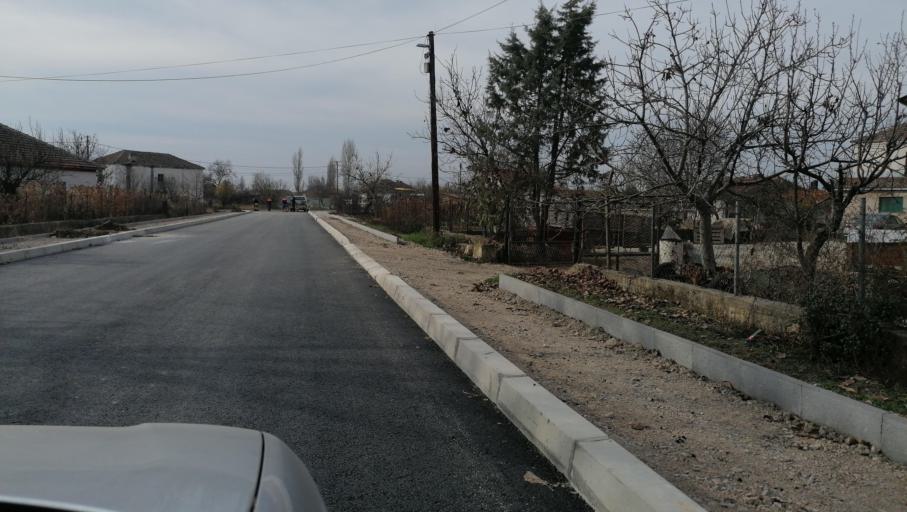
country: MK
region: Cesinovo-Oblesevo
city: Cesinovo
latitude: 41.8727
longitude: 22.2926
